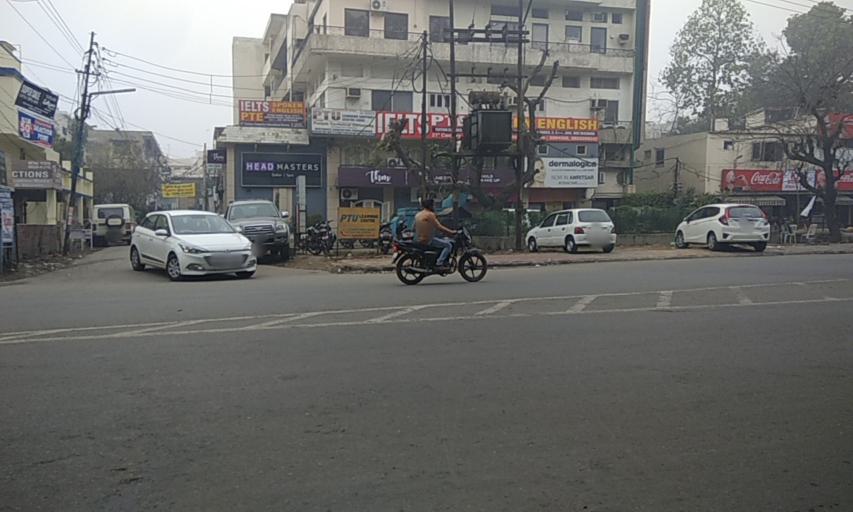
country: IN
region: Punjab
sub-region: Amritsar
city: Amritsar
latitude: 31.6414
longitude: 74.8670
